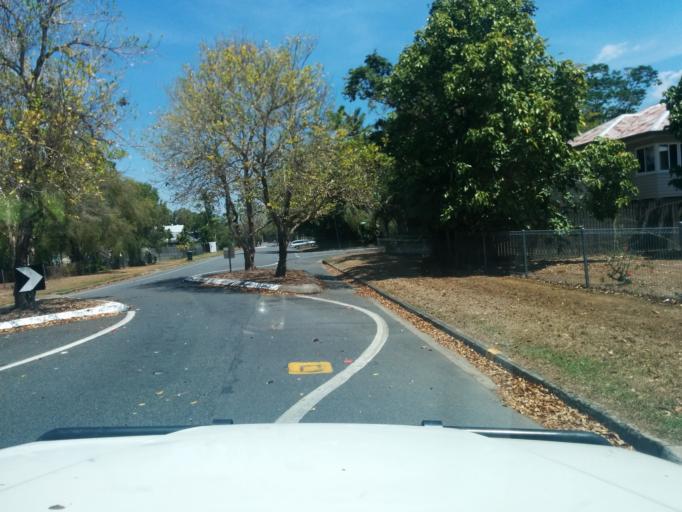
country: AU
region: Queensland
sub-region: Cairns
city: Woree
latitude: -16.9453
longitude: 145.7349
